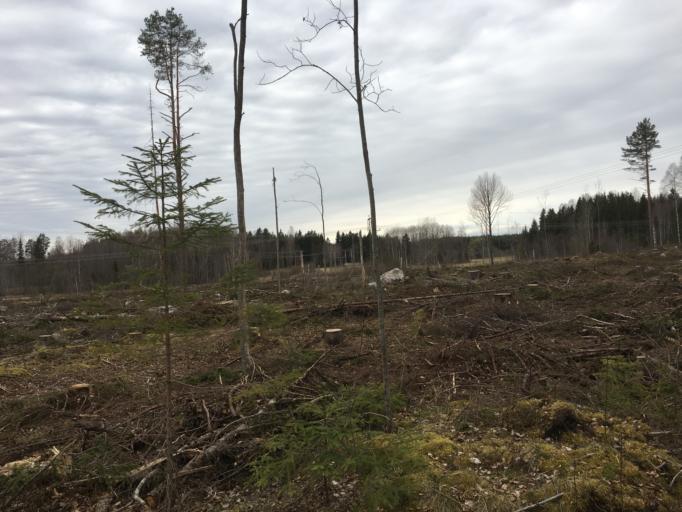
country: SE
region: Gaevleborg
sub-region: Hofors Kommun
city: Hofors
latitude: 60.5172
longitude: 16.4683
